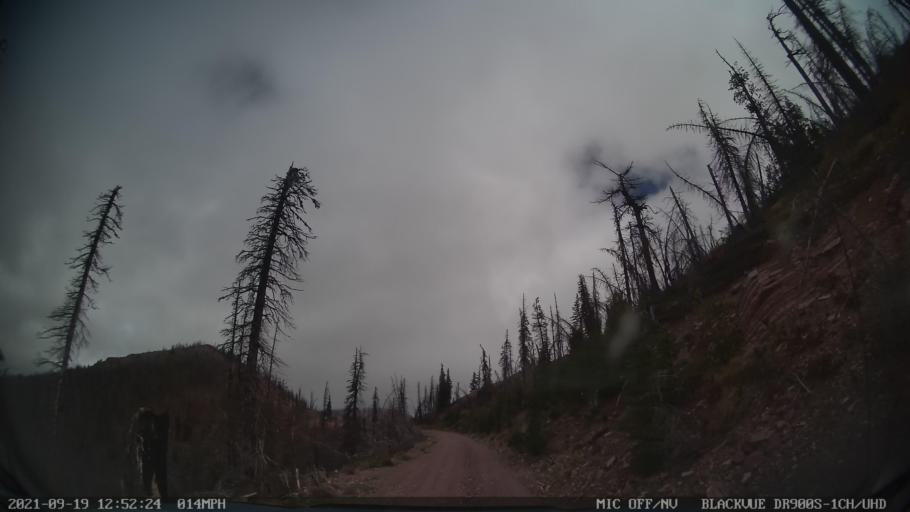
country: US
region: Montana
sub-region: Missoula County
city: Seeley Lake
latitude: 47.1927
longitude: -113.3570
